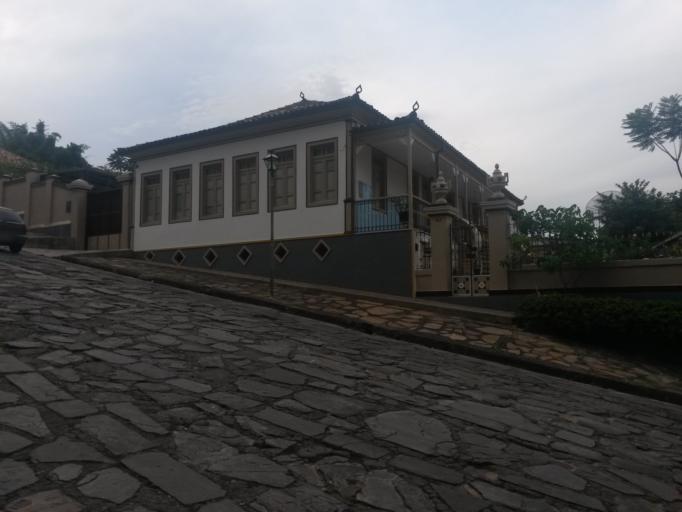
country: BR
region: Minas Gerais
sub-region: Diamantina
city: Diamantina
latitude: -18.2447
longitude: -43.5997
